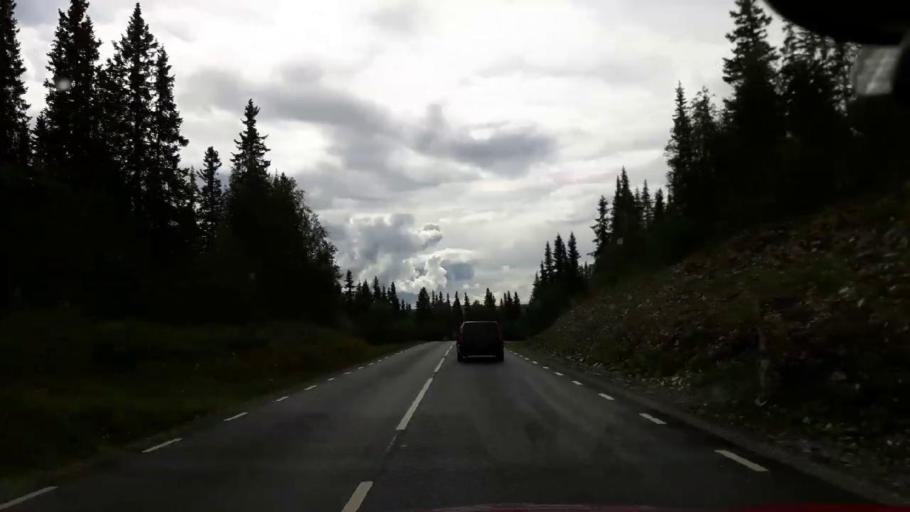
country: NO
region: Nord-Trondelag
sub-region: Royrvik
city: Royrvik
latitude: 64.8332
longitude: 14.1272
